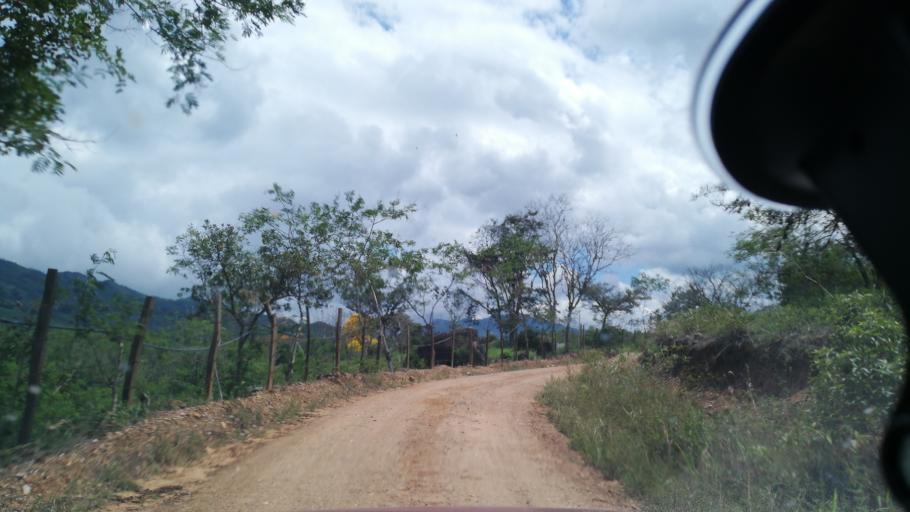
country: CO
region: Cundinamarca
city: Quipile
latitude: 4.7964
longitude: -74.6201
